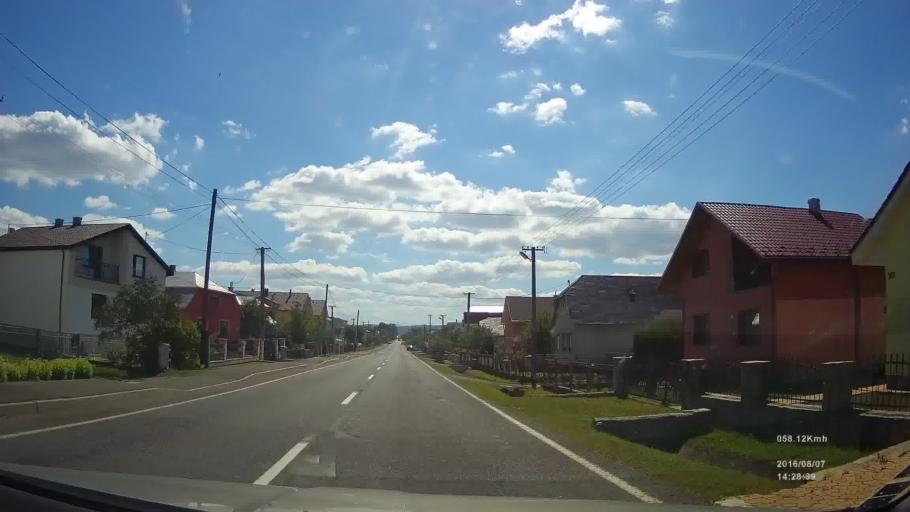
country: SK
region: Presovsky
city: Stropkov
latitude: 49.2480
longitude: 21.6841
